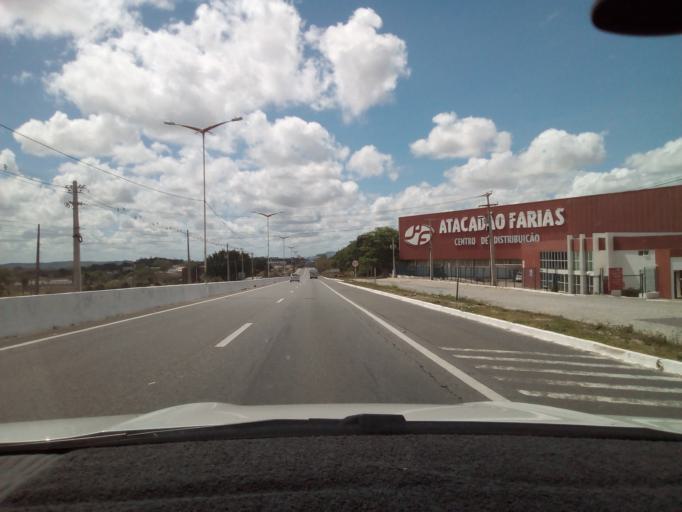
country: BR
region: Paraiba
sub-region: Campina Grande
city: Campina Grande
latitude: -7.2421
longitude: -35.8579
